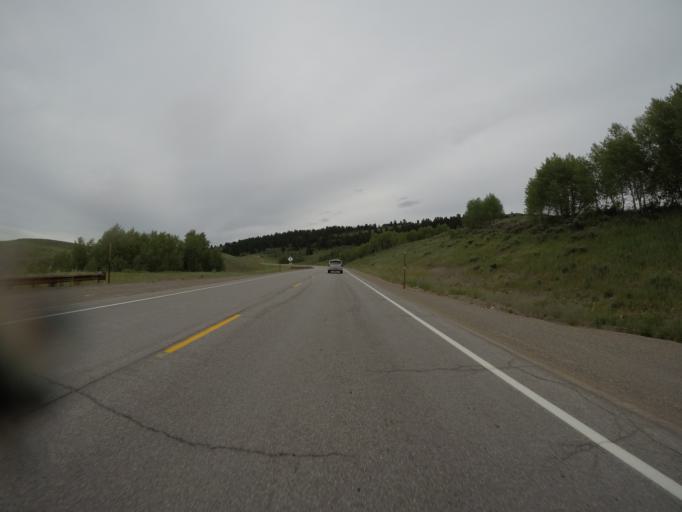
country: US
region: Wyoming
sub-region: Lincoln County
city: Afton
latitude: 42.4909
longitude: -110.9147
